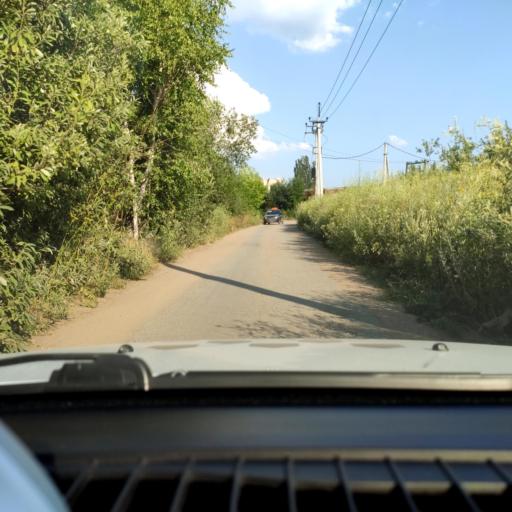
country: RU
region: Perm
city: Perm
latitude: 58.0290
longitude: 56.2374
